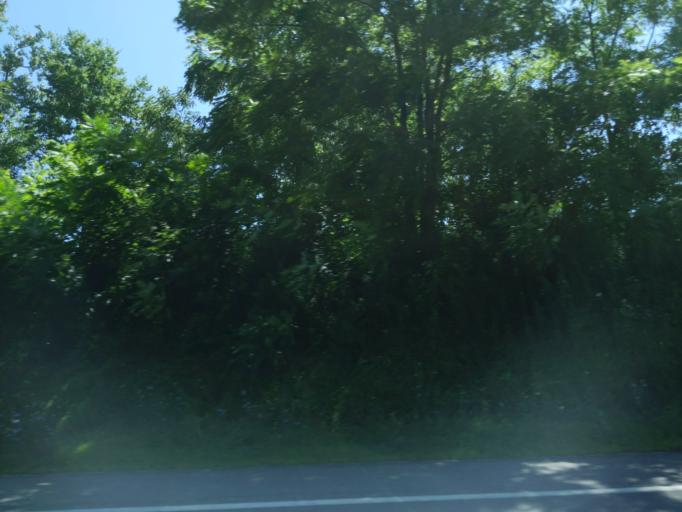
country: US
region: Wisconsin
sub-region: Vernon County
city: Westby
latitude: 43.6988
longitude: -91.0403
